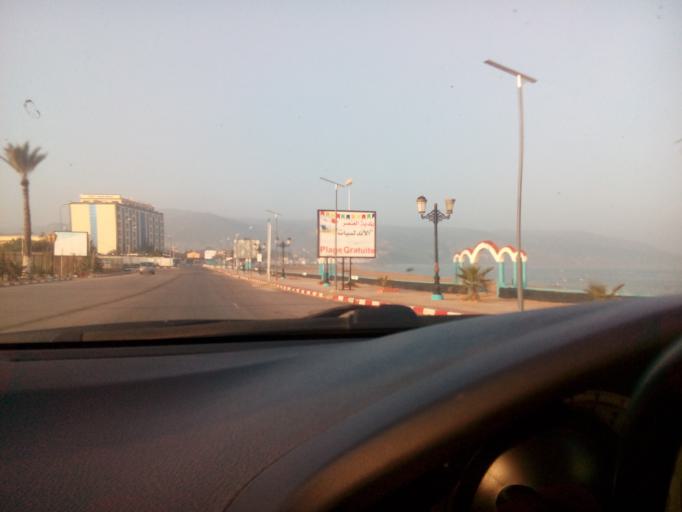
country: DZ
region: Oran
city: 'Ain el Turk
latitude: 35.7068
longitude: -0.8835
